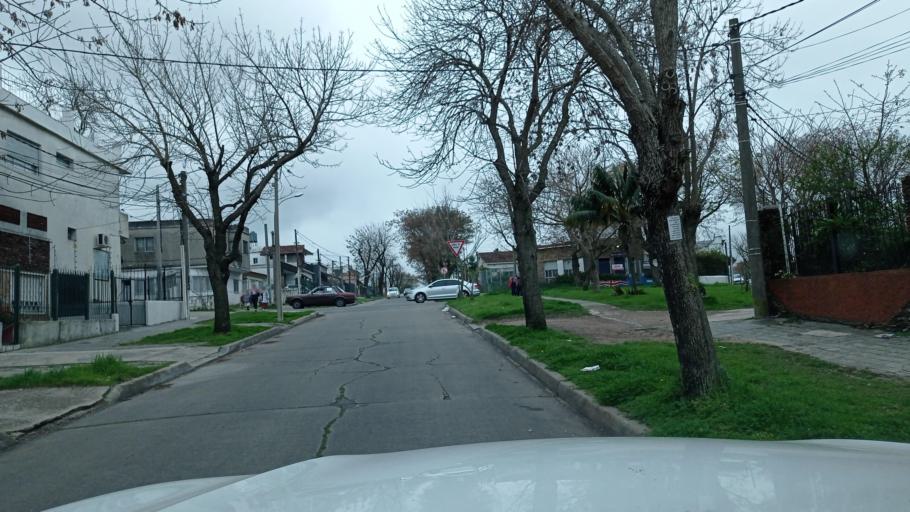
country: UY
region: Montevideo
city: Montevideo
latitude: -34.8466
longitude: -56.2088
